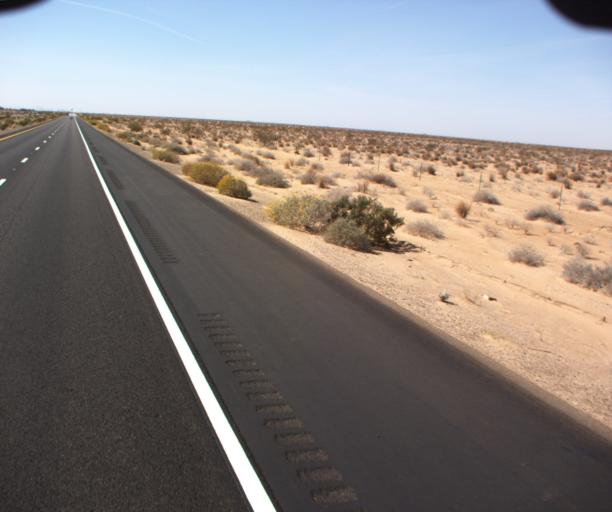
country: US
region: Arizona
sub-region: Yuma County
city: Somerton
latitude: 32.4954
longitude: -114.6177
